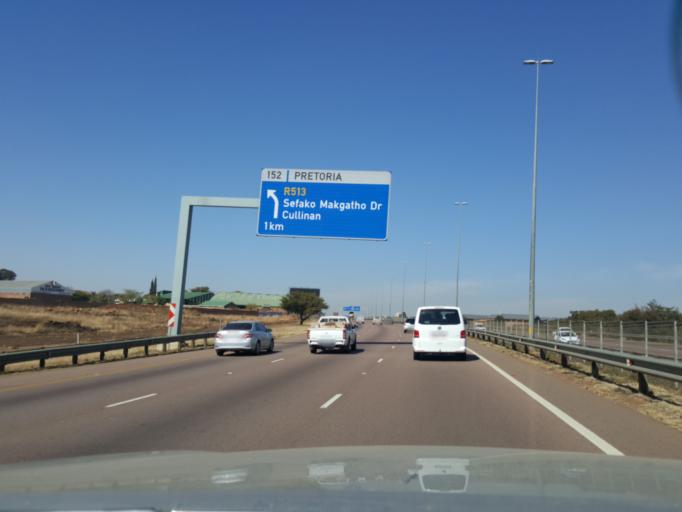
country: ZA
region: Gauteng
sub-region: City of Tshwane Metropolitan Municipality
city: Pretoria
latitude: -25.6717
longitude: 28.2733
